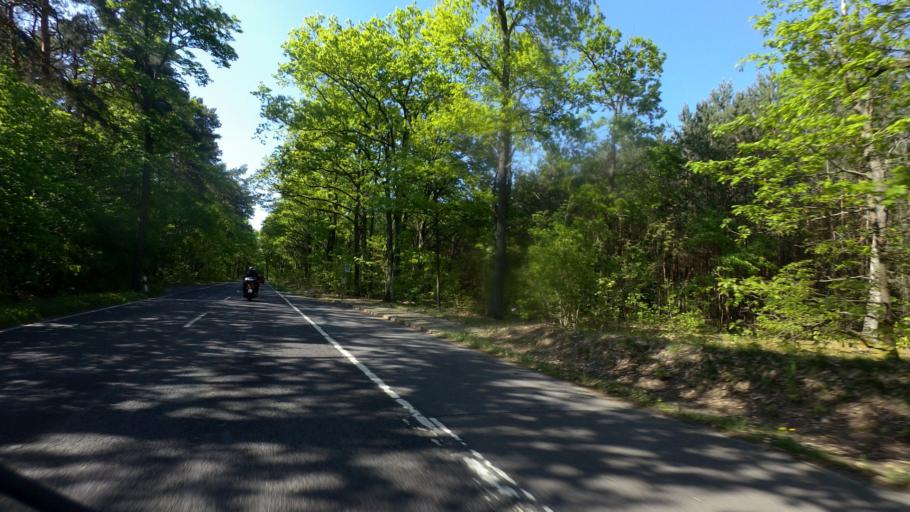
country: DE
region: Brandenburg
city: Bestensee
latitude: 52.2258
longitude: 13.6753
